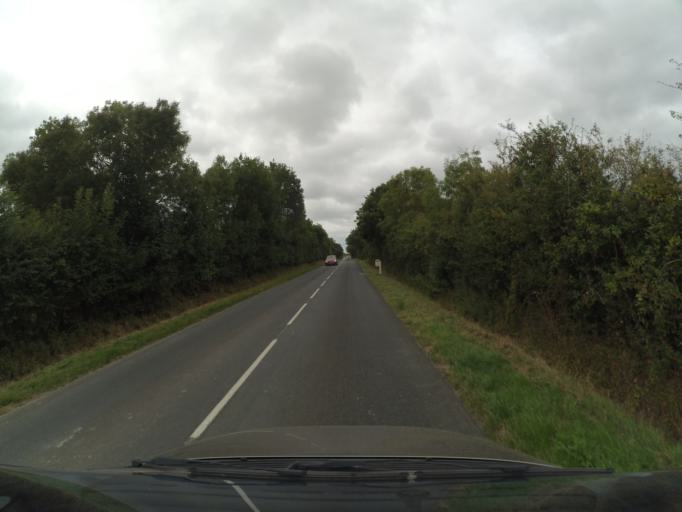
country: FR
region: Pays de la Loire
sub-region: Departement de la Vendee
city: Triaize
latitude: 46.4160
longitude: -1.2912
